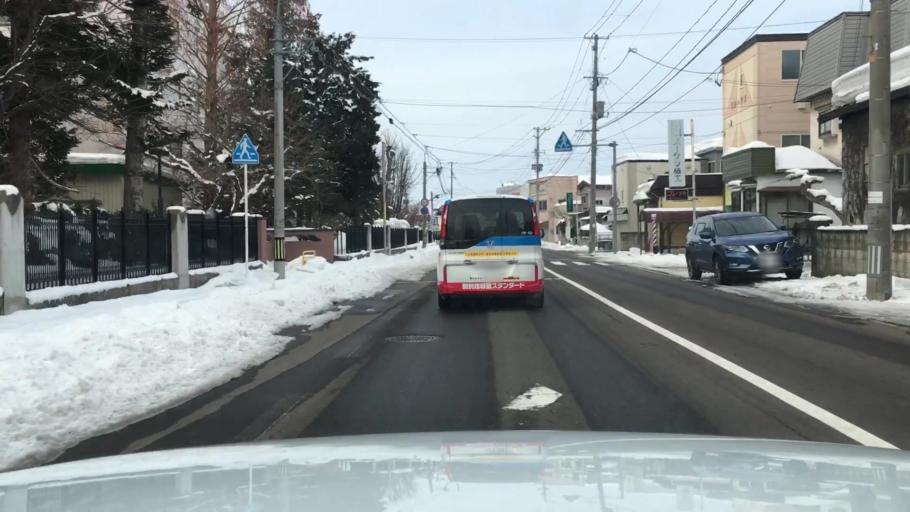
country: JP
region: Aomori
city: Hirosaki
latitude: 40.5869
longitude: 140.4747
